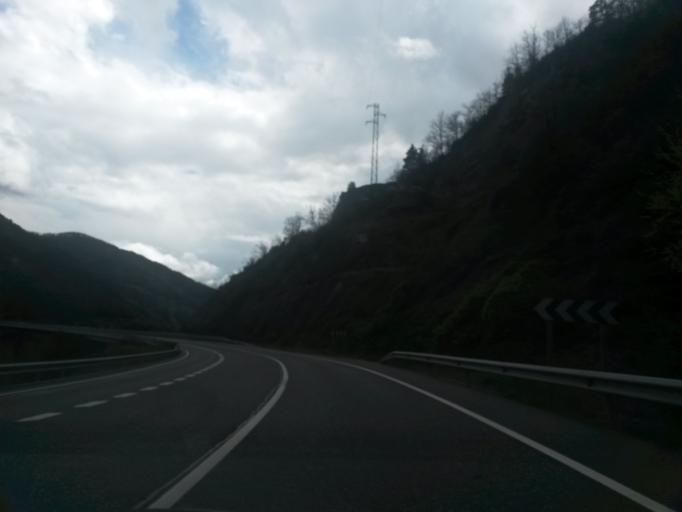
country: ES
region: Catalonia
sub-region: Provincia de Barcelona
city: Baga
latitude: 42.2847
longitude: 1.8500
